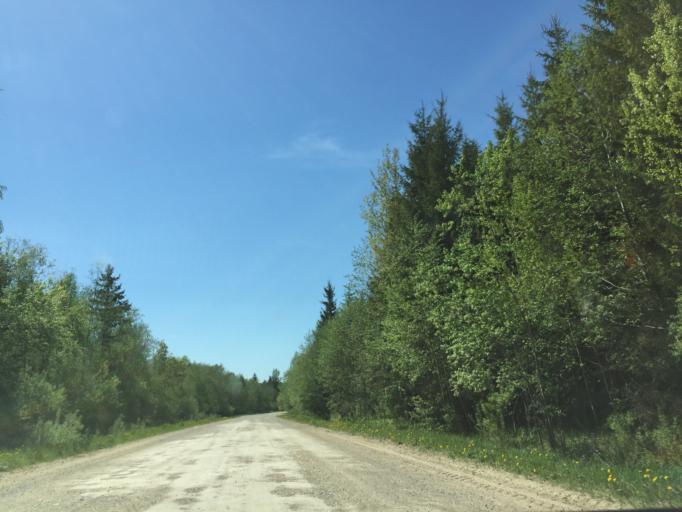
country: LV
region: Kegums
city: Kegums
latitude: 56.8709
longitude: 24.7756
